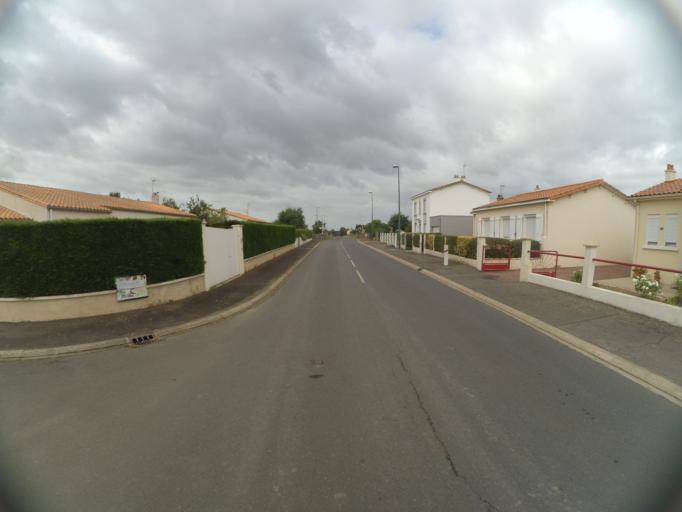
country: FR
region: Pays de la Loire
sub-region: Departement de la Vendee
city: Cugand
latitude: 47.0600
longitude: -1.2572
